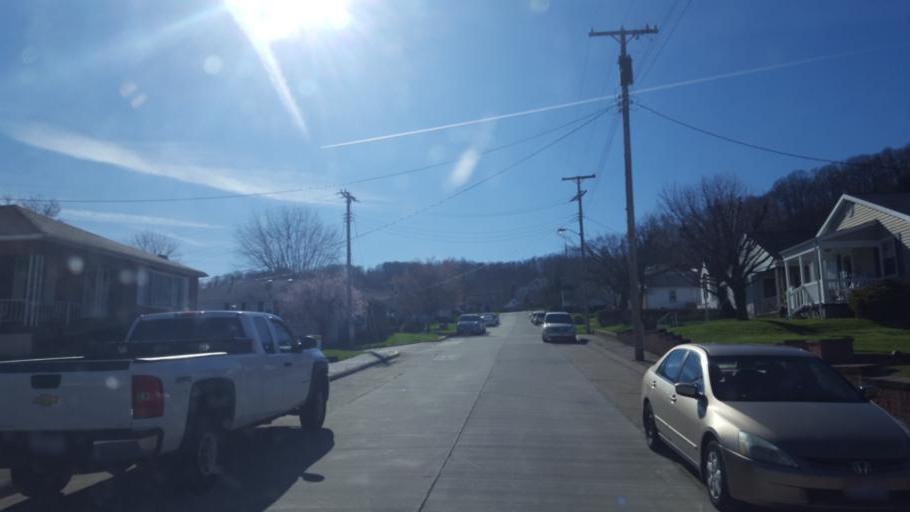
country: US
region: Ohio
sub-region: Jefferson County
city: Toronto
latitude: 40.4549
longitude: -80.6116
